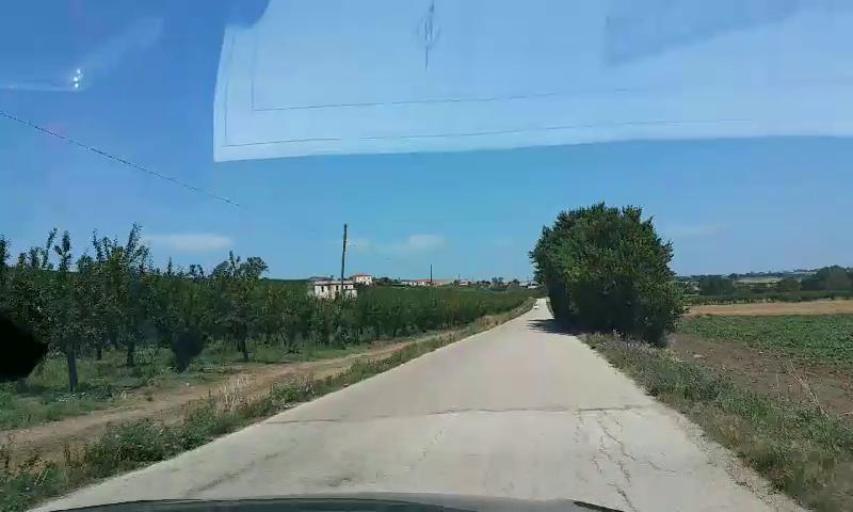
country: IT
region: Molise
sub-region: Provincia di Campobasso
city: San Giacomo degli Schiavoni
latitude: 41.9689
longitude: 14.9004
